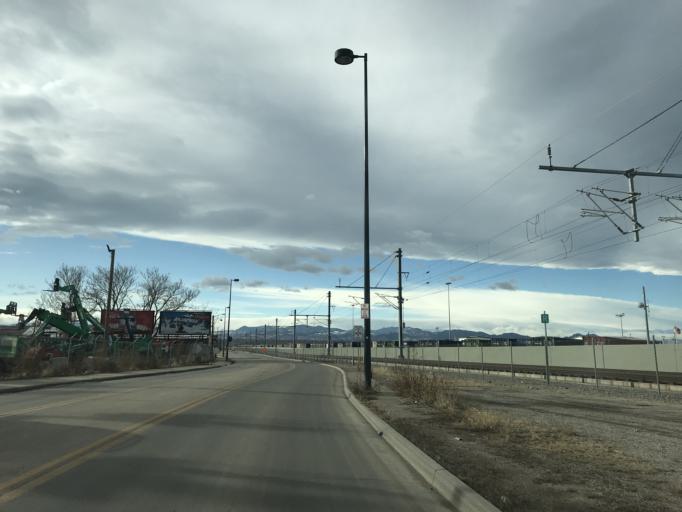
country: US
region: Colorado
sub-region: Denver County
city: Denver
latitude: 39.7728
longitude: -104.9604
